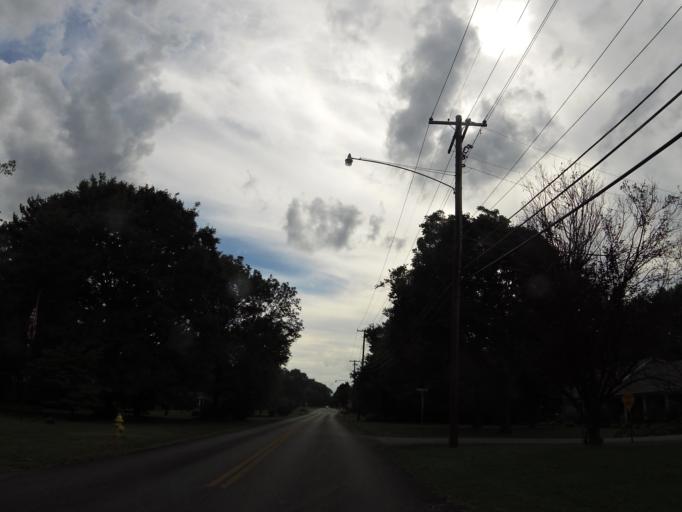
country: US
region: Kentucky
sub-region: Christian County
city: Hopkinsville
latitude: 36.8492
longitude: -87.5098
